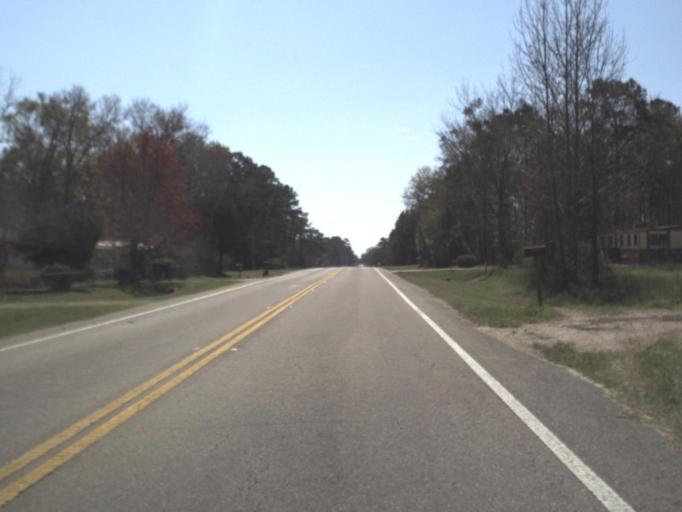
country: US
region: Florida
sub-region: Jefferson County
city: Monticello
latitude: 30.3992
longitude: -84.0176
